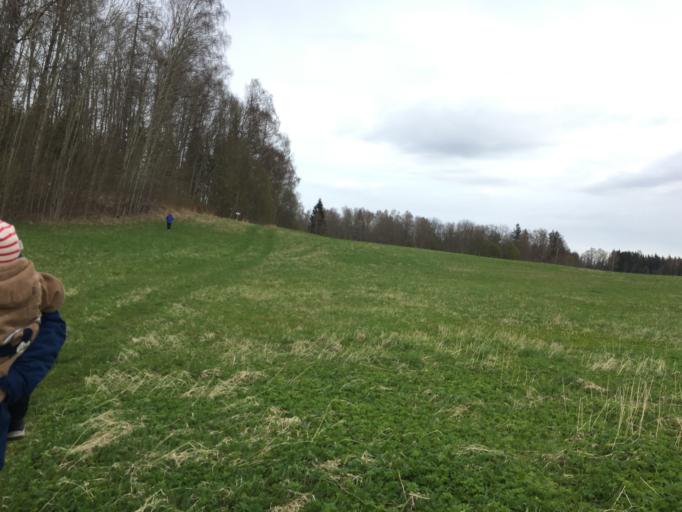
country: LV
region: Amatas Novads
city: Drabesi
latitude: 57.2590
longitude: 25.3006
